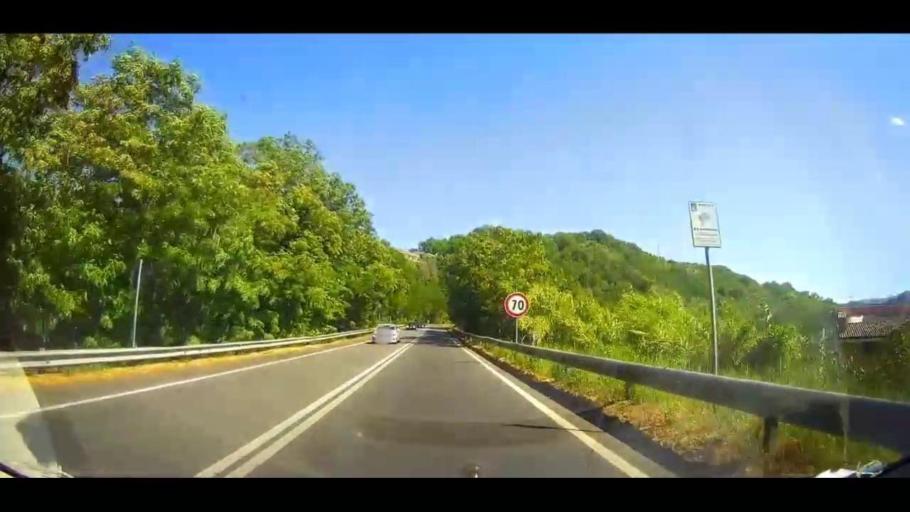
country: IT
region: Calabria
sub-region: Provincia di Cosenza
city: Cosenza
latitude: 39.3075
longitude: 16.2628
